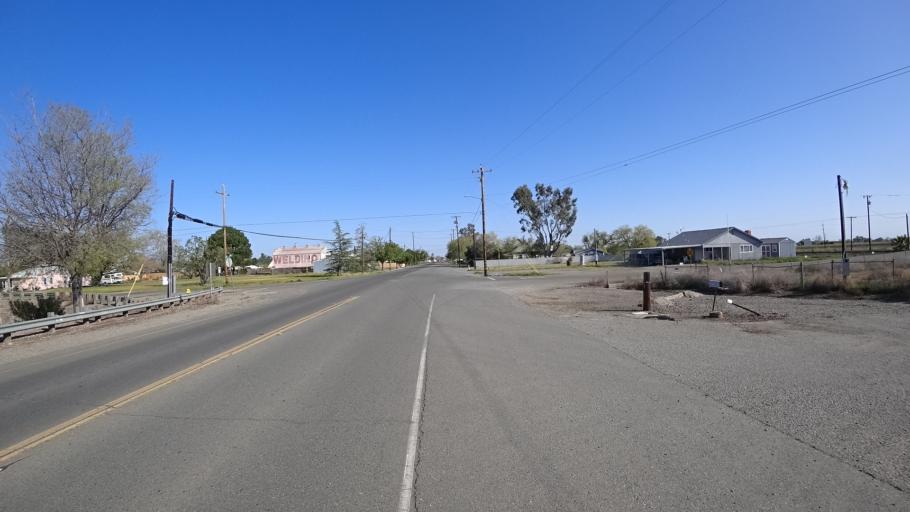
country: US
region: California
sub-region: Glenn County
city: Willows
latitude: 39.5093
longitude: -122.1938
